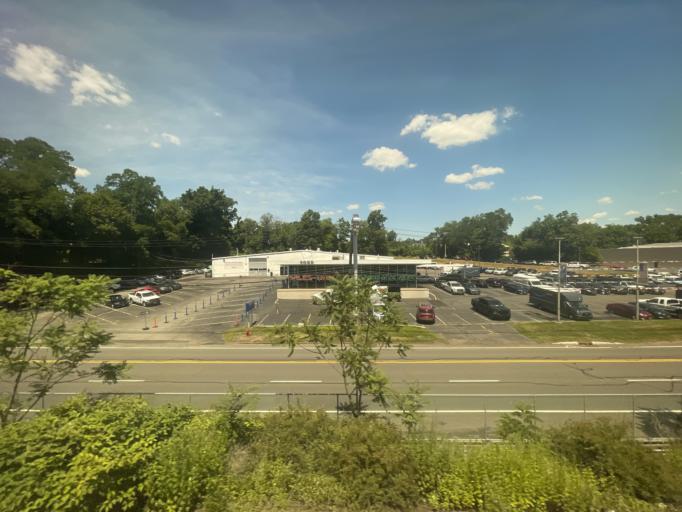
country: US
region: New Jersey
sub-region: Middlesex County
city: Avenel
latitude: 40.5905
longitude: -74.2958
